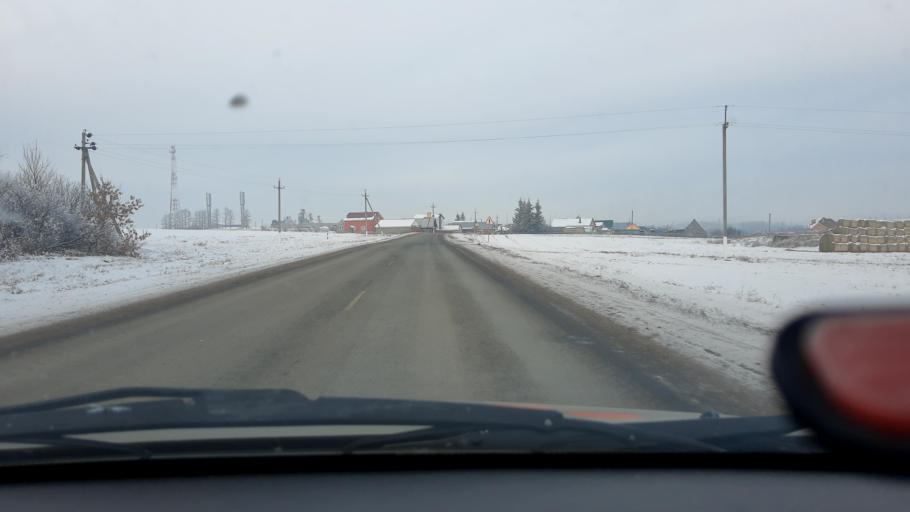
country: RU
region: Bashkortostan
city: Avdon
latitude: 54.4091
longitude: 55.8055
